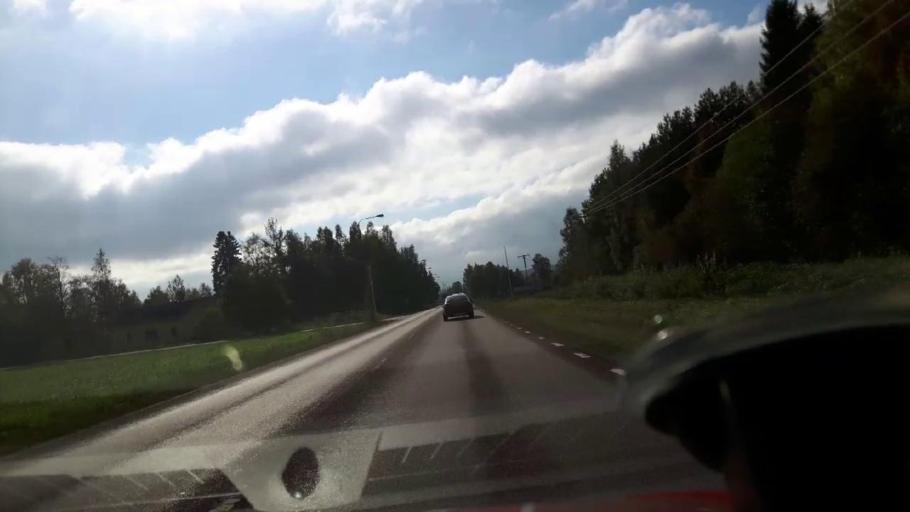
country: SE
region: Gaevleborg
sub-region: Bollnas Kommun
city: Arbra
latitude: 61.5231
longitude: 16.3639
